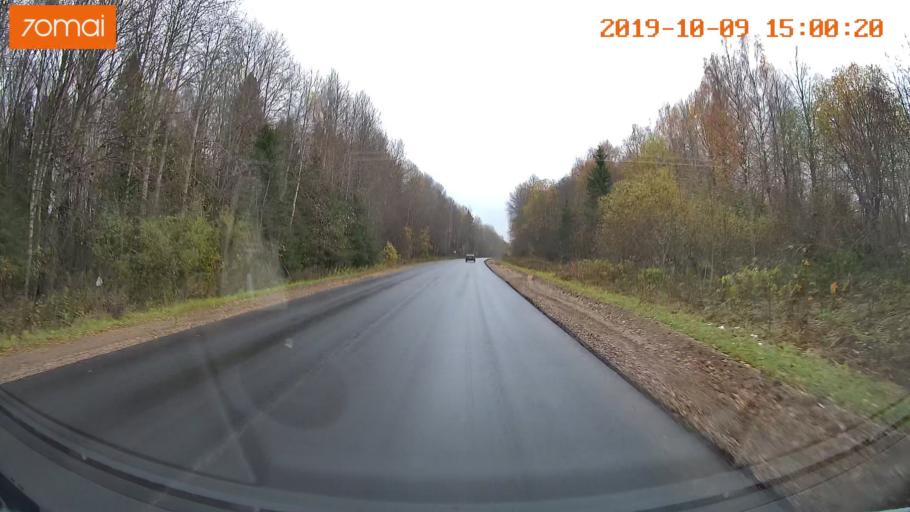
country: RU
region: Kostroma
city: Chistyye Bory
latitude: 58.3106
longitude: 41.6774
